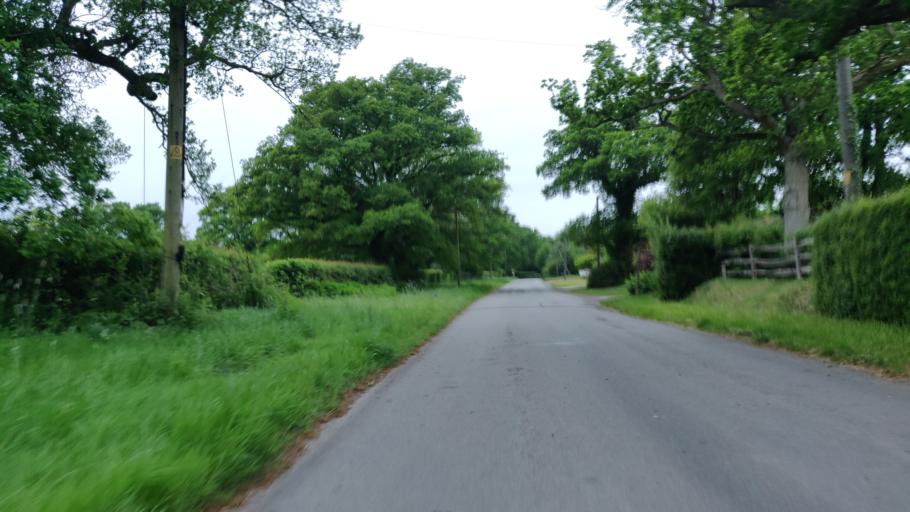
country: GB
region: England
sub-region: West Sussex
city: Southwater
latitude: 51.0108
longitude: -0.3240
